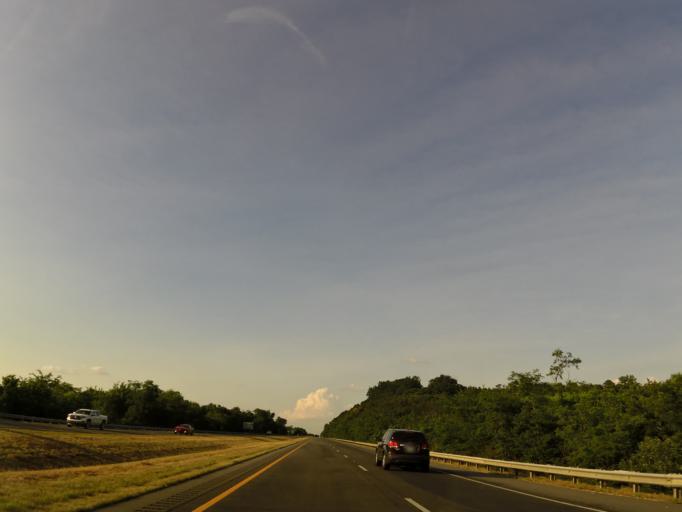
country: US
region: Alabama
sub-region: DeKalb County
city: Fort Payne
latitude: 34.4470
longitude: -85.7379
